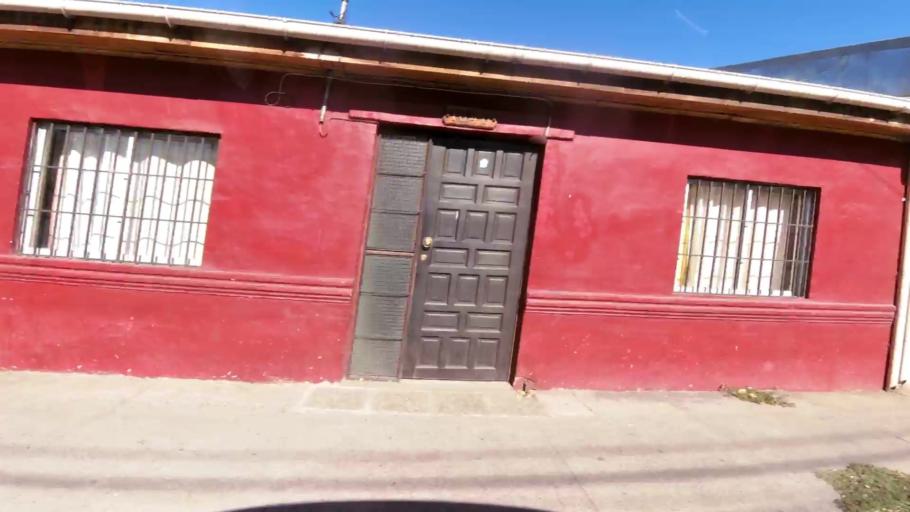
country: CL
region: O'Higgins
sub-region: Provincia de Colchagua
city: Chimbarongo
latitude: -34.5801
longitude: -70.9947
